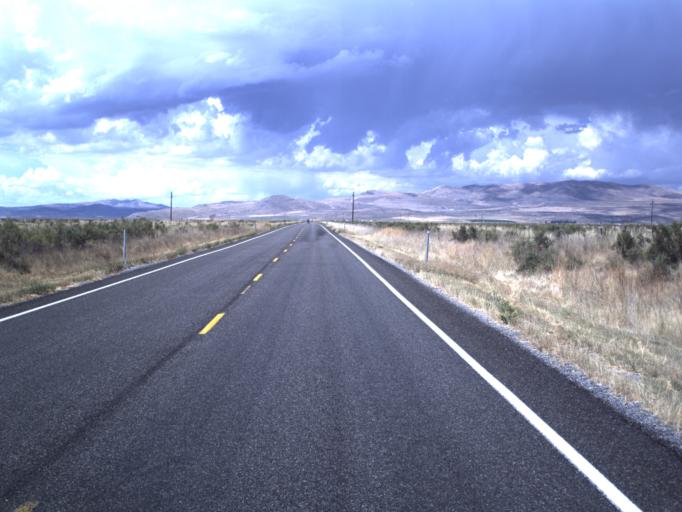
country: US
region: Utah
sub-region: Box Elder County
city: Tremonton
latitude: 41.5891
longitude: -112.2711
